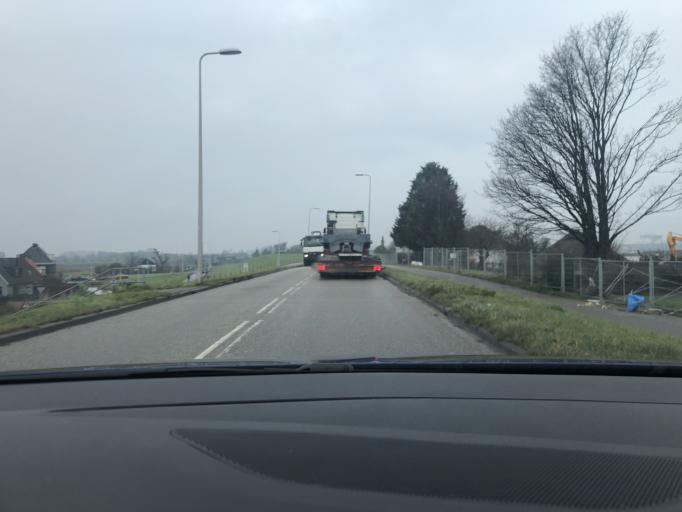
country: NL
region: South Holland
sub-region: Gemeente Hendrik-Ido-Ambacht
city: Hendrik-Ido-Ambacht
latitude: 51.8352
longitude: 4.6589
